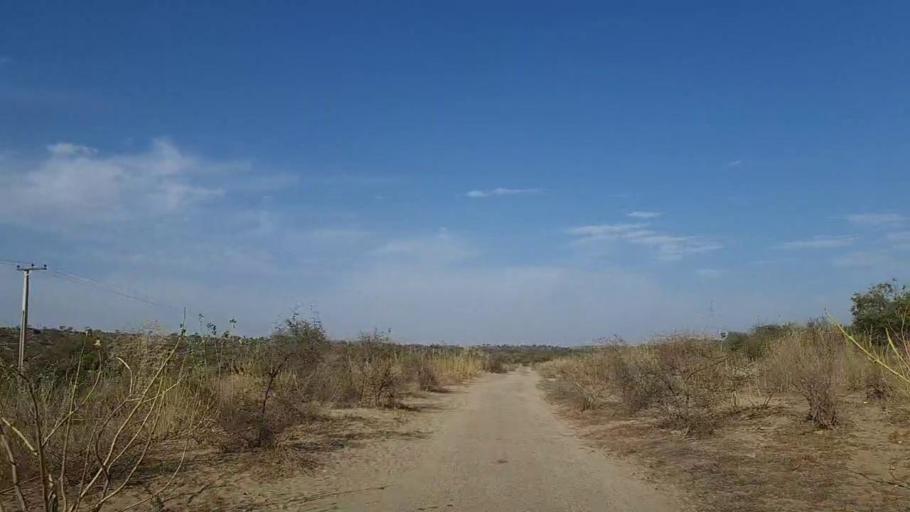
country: PK
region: Sindh
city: Naukot
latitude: 24.8491
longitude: 69.5180
